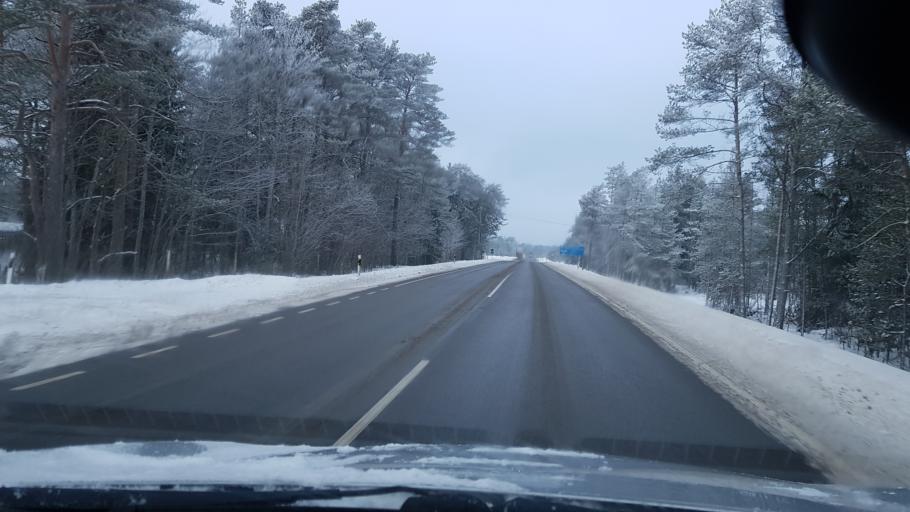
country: EE
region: Harju
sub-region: Keila linn
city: Keila
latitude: 59.3346
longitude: 24.2868
